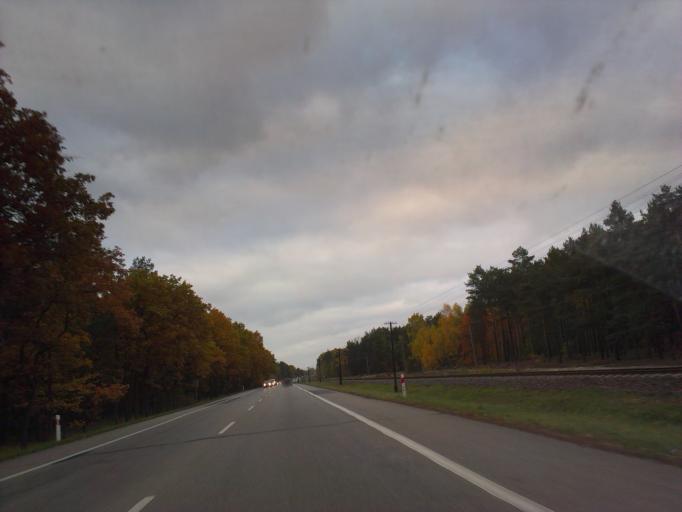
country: PL
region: Kujawsko-Pomorskie
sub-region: Powiat torunski
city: Lysomice
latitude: 53.0657
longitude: 18.6175
